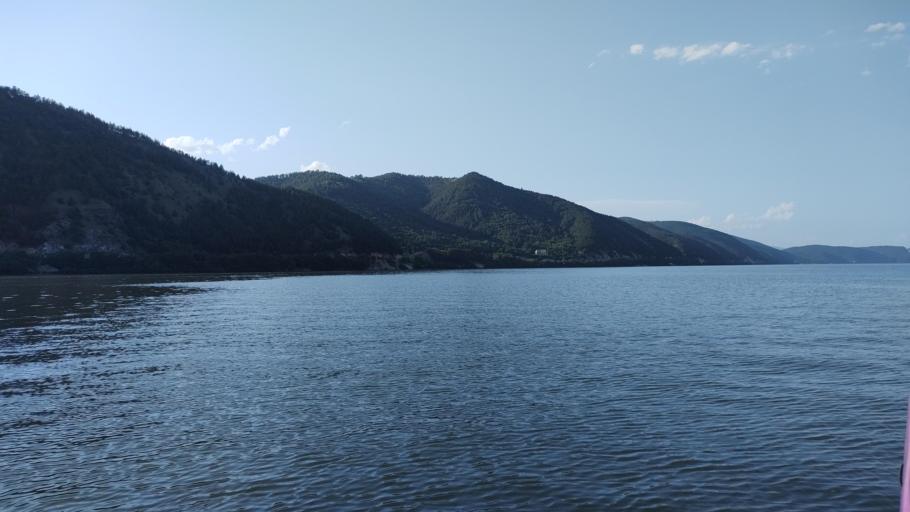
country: RO
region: Mehedinti
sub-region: Comuna Svinita
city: Svinita
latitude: 44.5084
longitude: 22.1967
